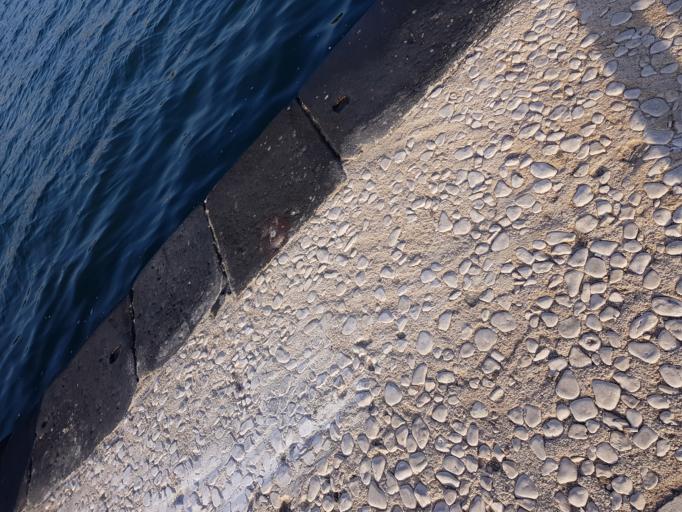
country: IT
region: Apulia
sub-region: Provincia di Brindisi
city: Brindisi
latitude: 40.6424
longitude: 17.9448
